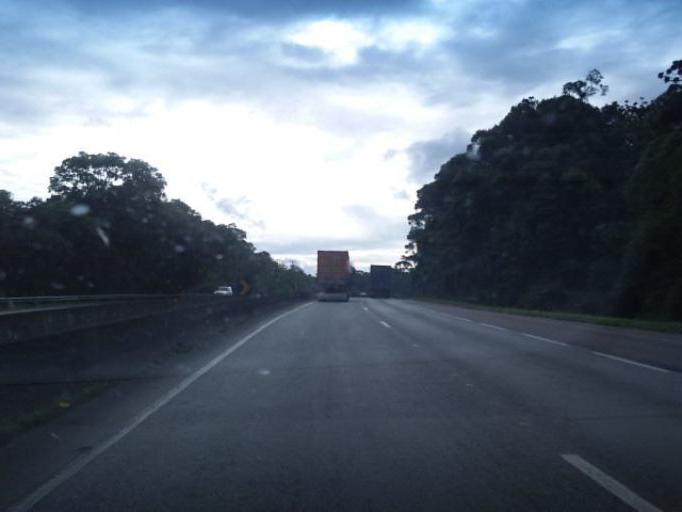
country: BR
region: Parana
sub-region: Campina Grande Do Sul
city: Campina Grande do Sul
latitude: -25.3077
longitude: -48.9798
